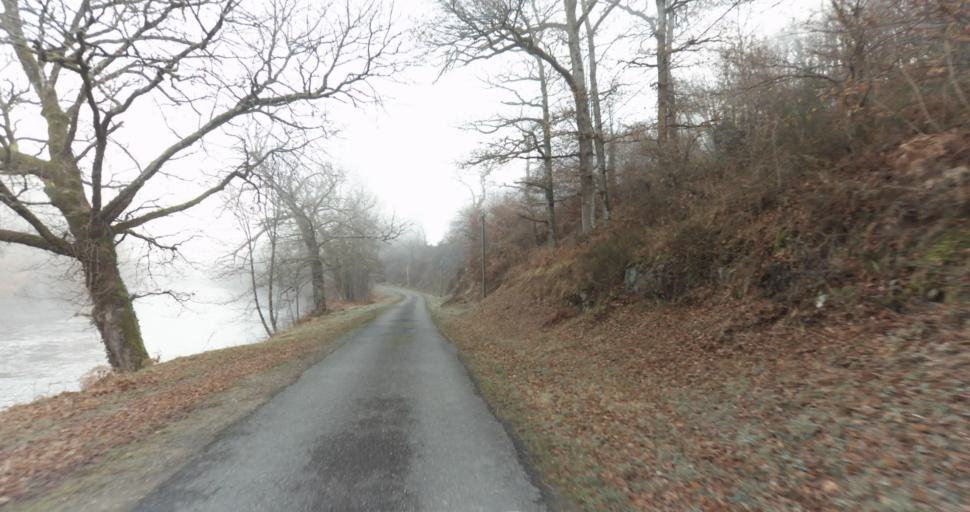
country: FR
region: Limousin
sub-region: Departement de la Haute-Vienne
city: Saint-Priest-sous-Aixe
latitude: 45.8162
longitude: 1.1197
